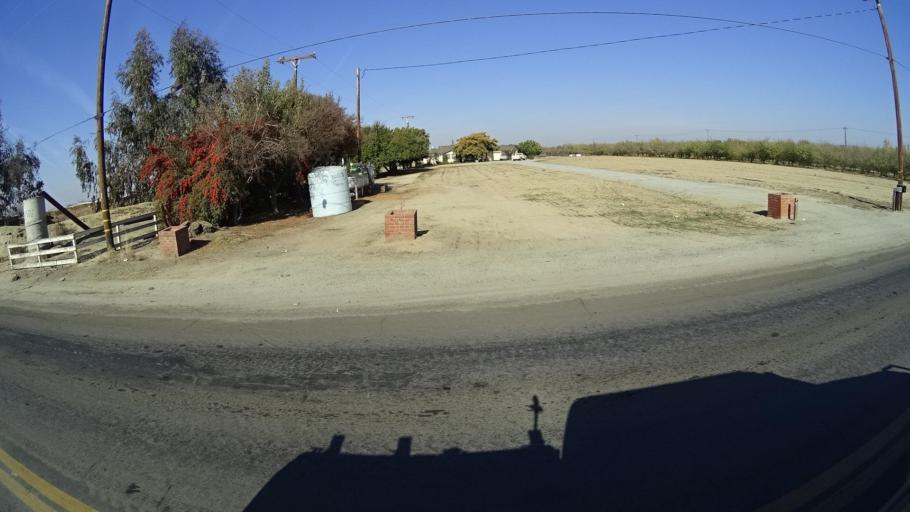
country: US
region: California
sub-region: Kern County
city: McFarland
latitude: 35.6892
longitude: -119.2244
